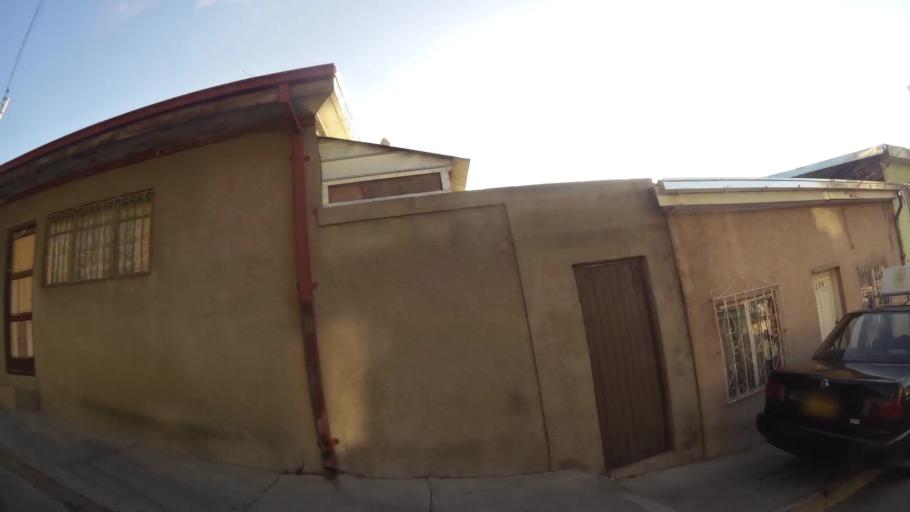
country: CL
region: Valparaiso
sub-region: Provincia de Valparaiso
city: Valparaiso
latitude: -33.0550
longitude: -71.6048
